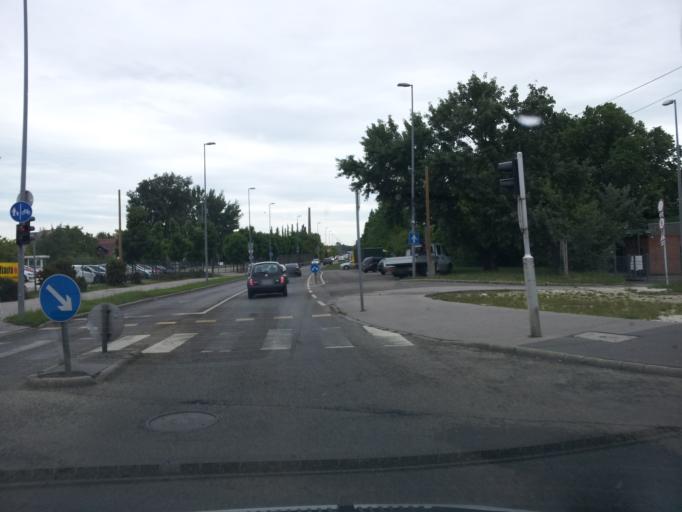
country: HU
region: Budapest
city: Budapest III. keruelet
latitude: 47.5526
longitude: 19.0481
